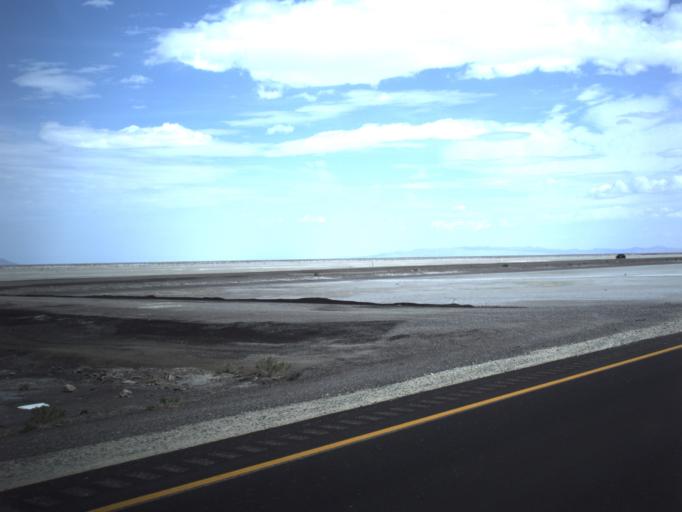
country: US
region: Utah
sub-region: Tooele County
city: Wendover
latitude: 40.7331
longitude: -113.5948
